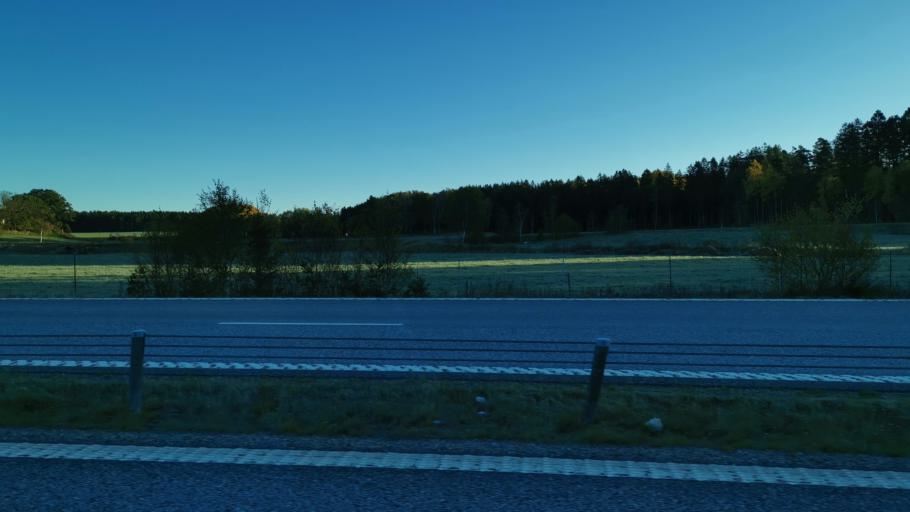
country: SE
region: Vaestra Goetaland
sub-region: Tanums Kommun
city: Tanumshede
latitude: 58.6197
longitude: 11.4510
